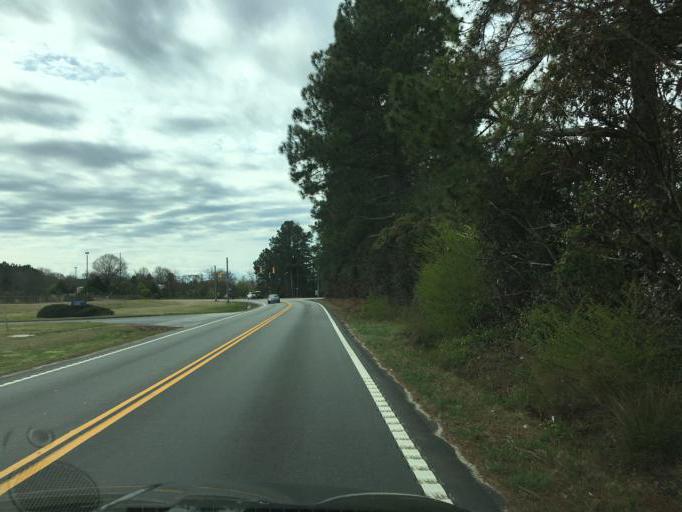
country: US
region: South Carolina
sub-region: Greenville County
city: Fountain Inn
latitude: 34.6868
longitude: -82.2194
